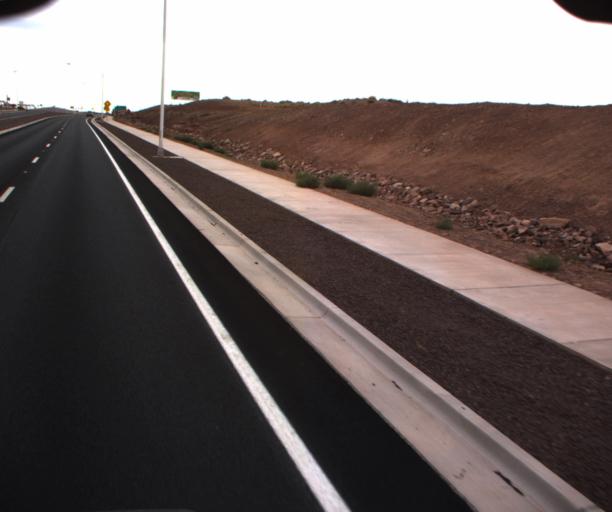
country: US
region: Arizona
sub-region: Coconino County
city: Tuba City
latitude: 35.8579
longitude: -111.4223
